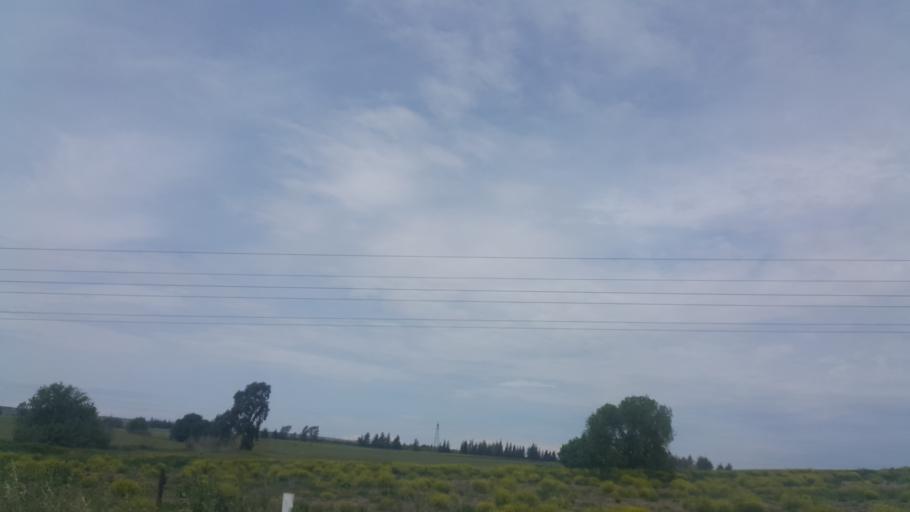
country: TR
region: Adana
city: Yakapinar
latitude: 37.0011
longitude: 35.6879
